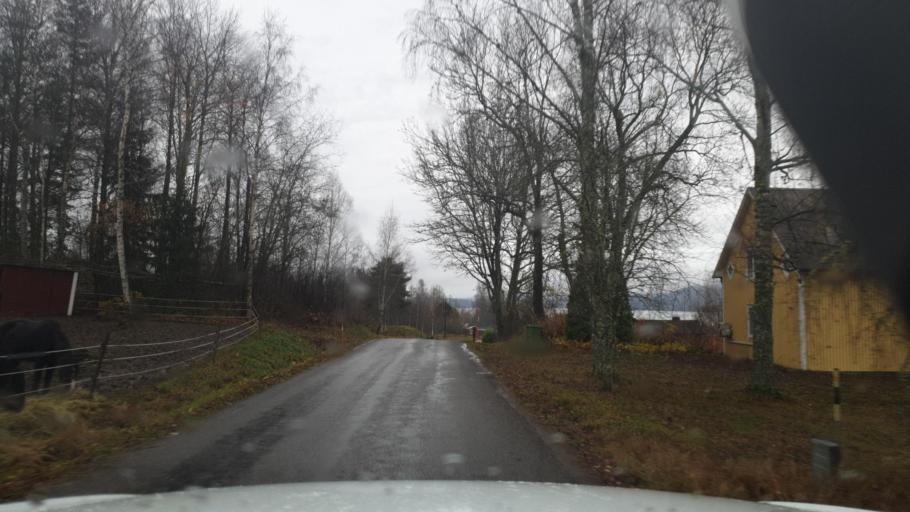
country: SE
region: Vaermland
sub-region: Eda Kommun
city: Amotfors
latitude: 59.7625
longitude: 12.4438
